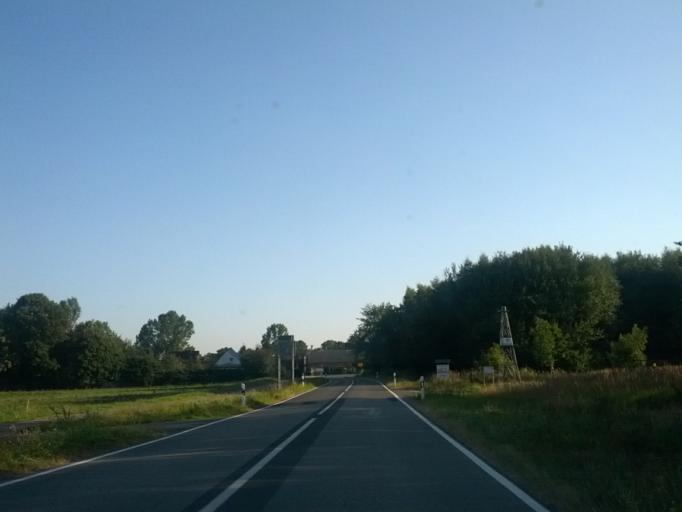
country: DE
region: Mecklenburg-Vorpommern
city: Brandshagen
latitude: 54.1886
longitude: 13.1820
